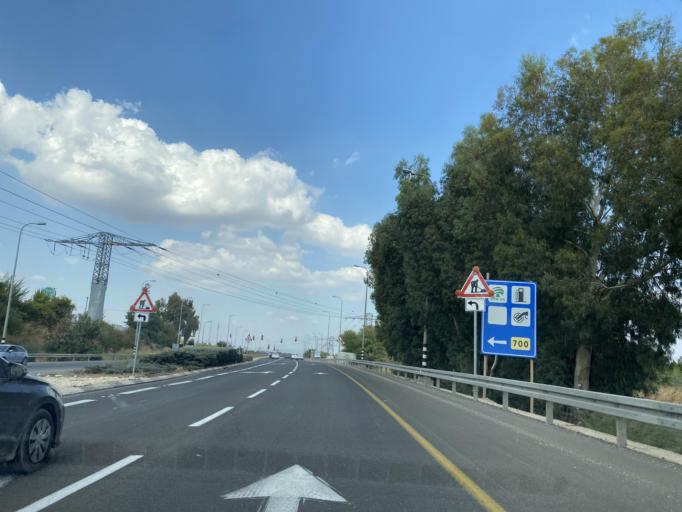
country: IL
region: Northern District
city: Rosh Pinna
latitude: 32.9801
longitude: 35.5571
